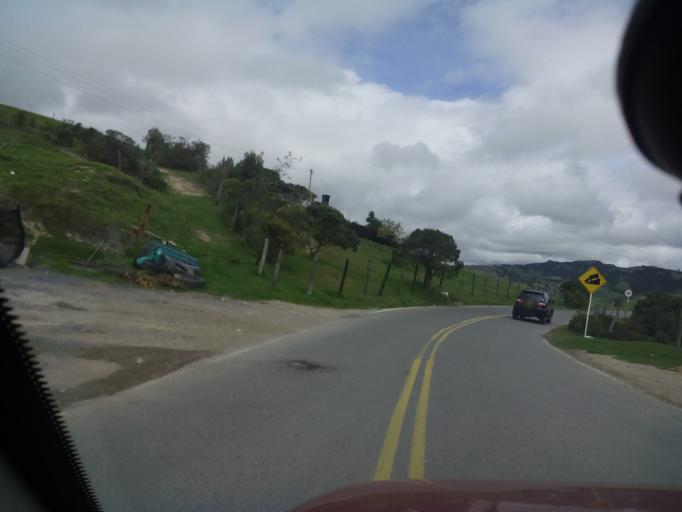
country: CO
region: Boyaca
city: Combita
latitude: 5.6360
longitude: -73.3463
